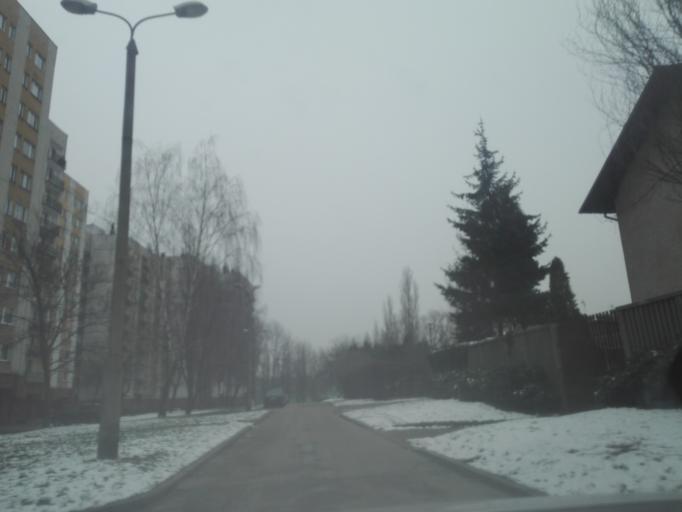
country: PL
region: Silesian Voivodeship
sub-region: Katowice
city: Katowice
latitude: 50.2478
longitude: 19.0318
